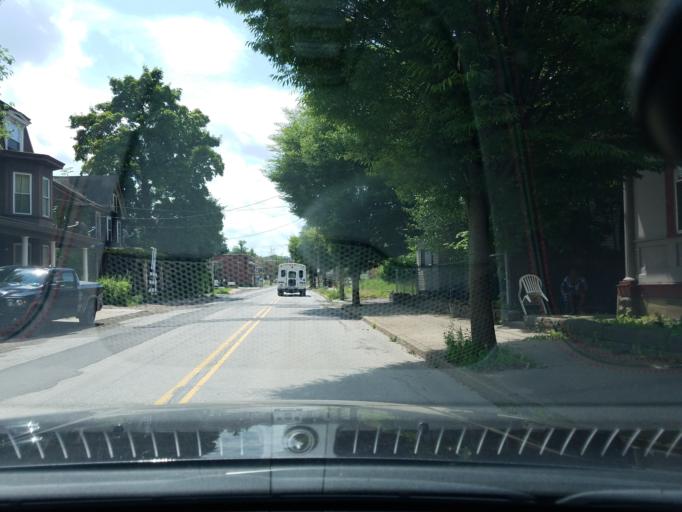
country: US
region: Pennsylvania
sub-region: Cambria County
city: Johnstown
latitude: 40.3187
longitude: -78.9184
